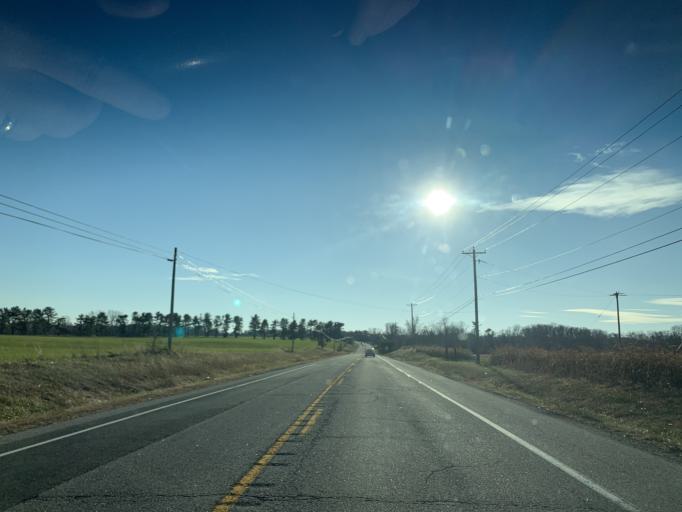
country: US
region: Delaware
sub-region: New Castle County
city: Middletown
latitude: 39.3831
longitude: -75.8756
